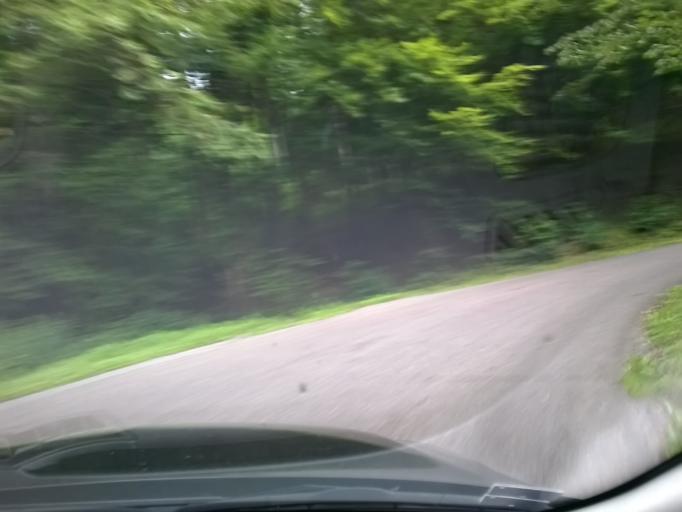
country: SK
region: Banskobystricky
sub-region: Okres Banska Bystrica
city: Banska Stiavnica
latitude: 48.4701
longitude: 18.8609
